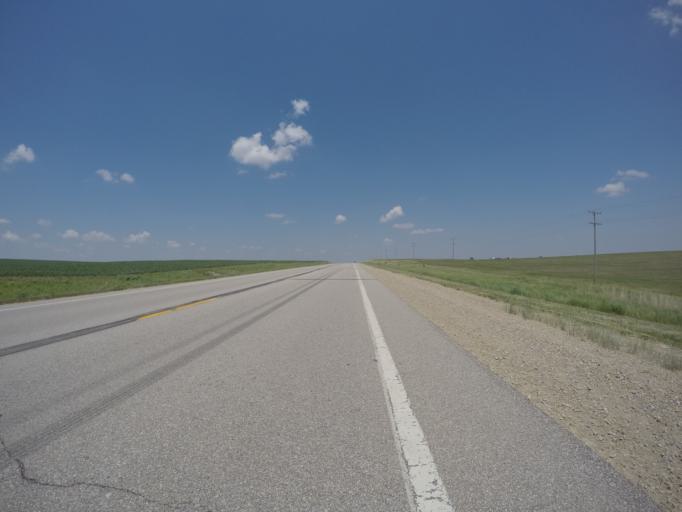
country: US
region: Kansas
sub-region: Doniphan County
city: Troy
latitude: 39.7484
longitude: -95.1438
